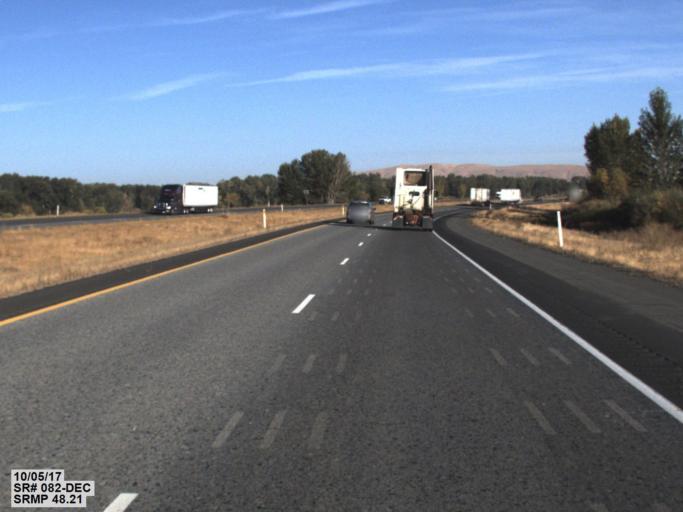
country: US
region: Washington
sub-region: Yakima County
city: Toppenish
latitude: 46.4321
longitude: -120.3439
